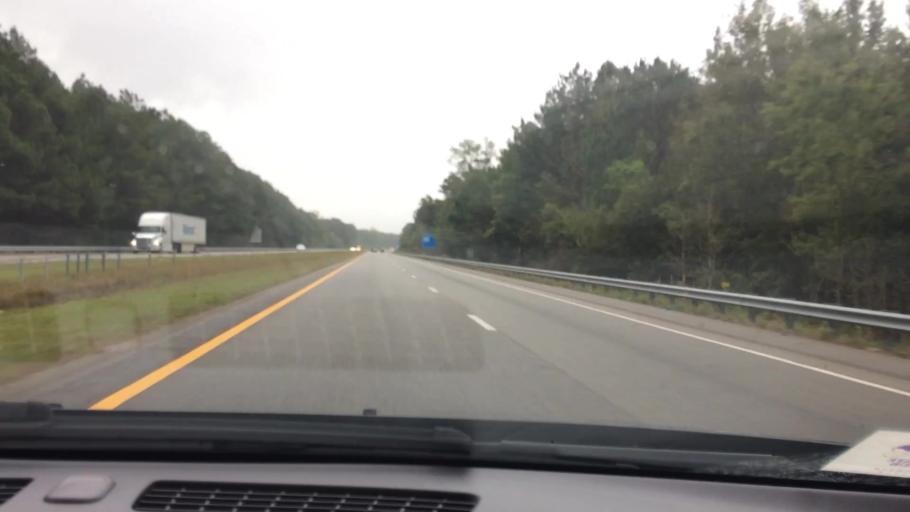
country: US
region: North Carolina
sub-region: Wilson County
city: Lucama
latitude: 35.7043
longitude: -77.9878
